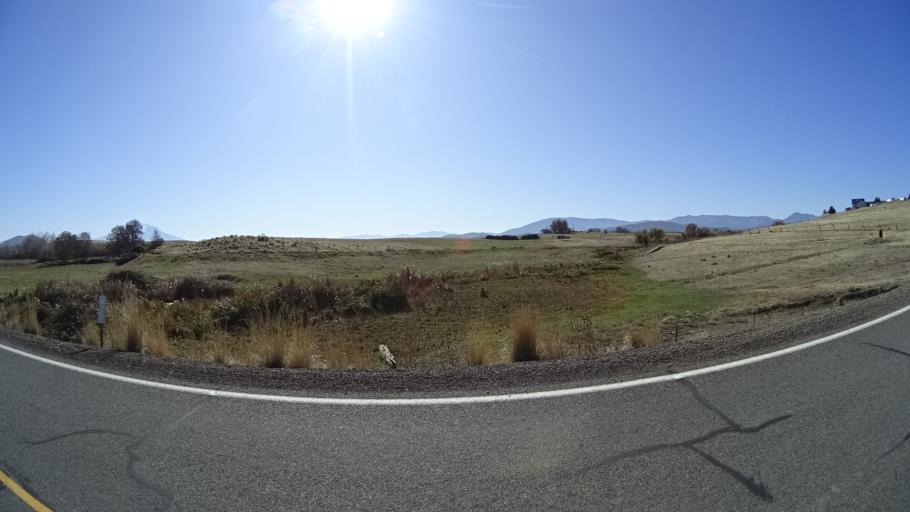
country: US
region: California
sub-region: Siskiyou County
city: Montague
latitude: 41.7456
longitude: -122.5775
